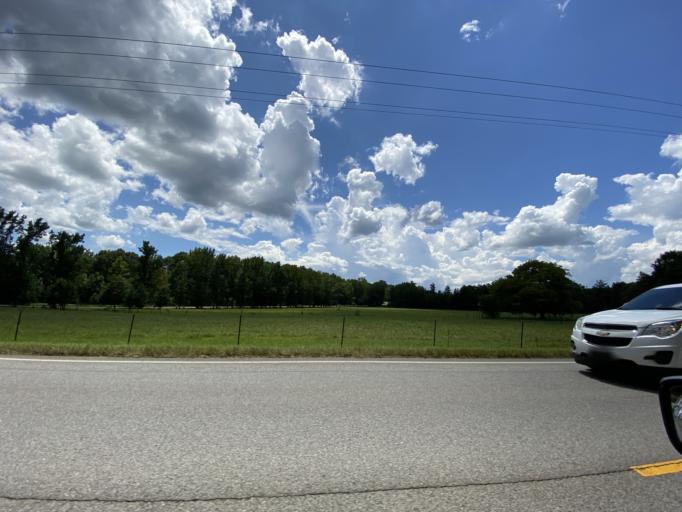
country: US
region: Alabama
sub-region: Lauderdale County
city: Underwood-Petersville
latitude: 34.9521
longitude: -87.8720
